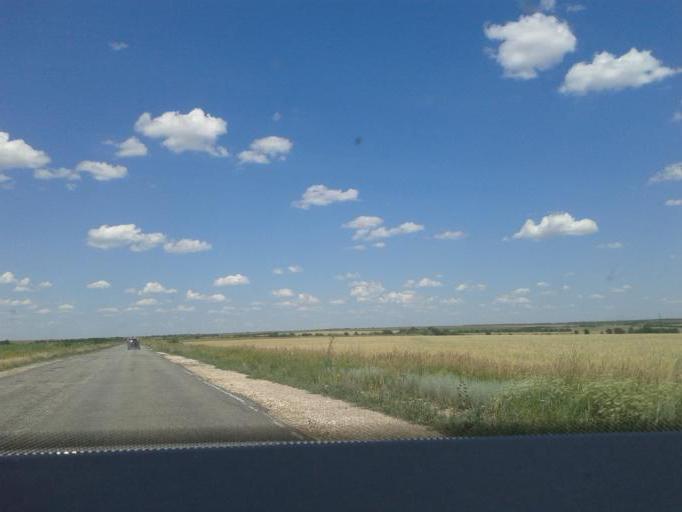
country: RU
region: Volgograd
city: Frolovo
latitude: 49.6570
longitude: 43.6196
